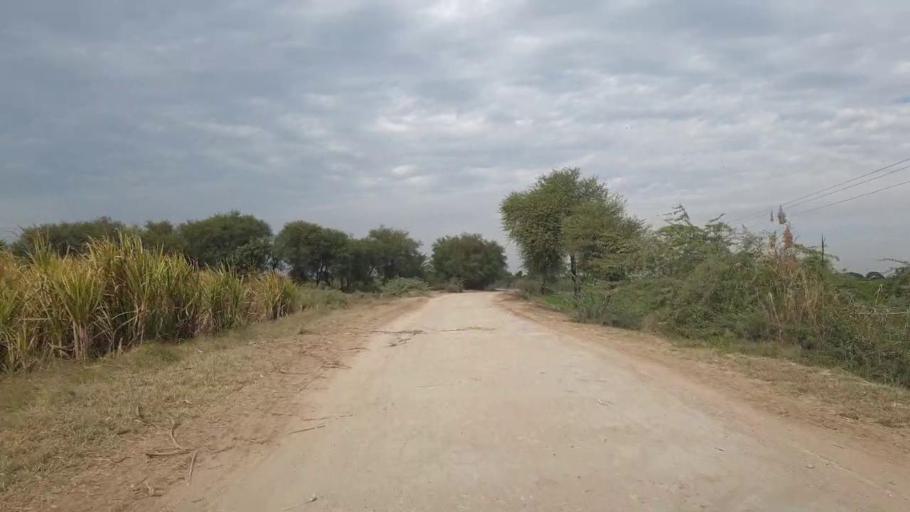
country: PK
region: Sindh
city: Sinjhoro
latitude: 26.0216
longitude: 68.8747
